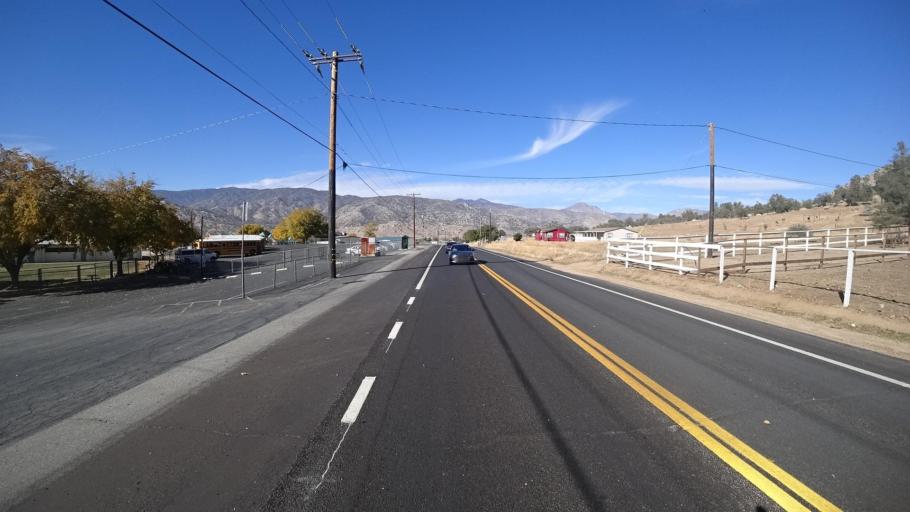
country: US
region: California
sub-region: Kern County
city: Lake Isabella
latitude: 35.6095
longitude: -118.4650
